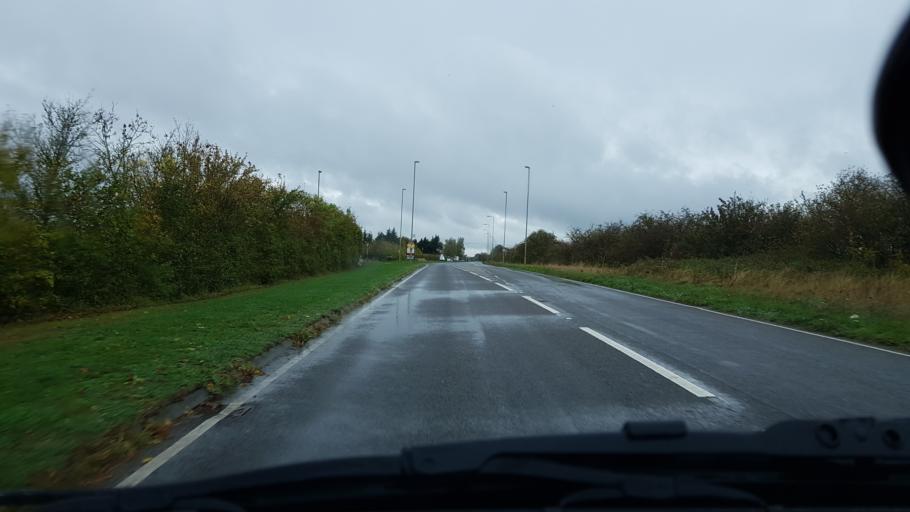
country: GB
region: England
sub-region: Oxfordshire
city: Ducklington
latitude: 51.7377
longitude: -1.4434
